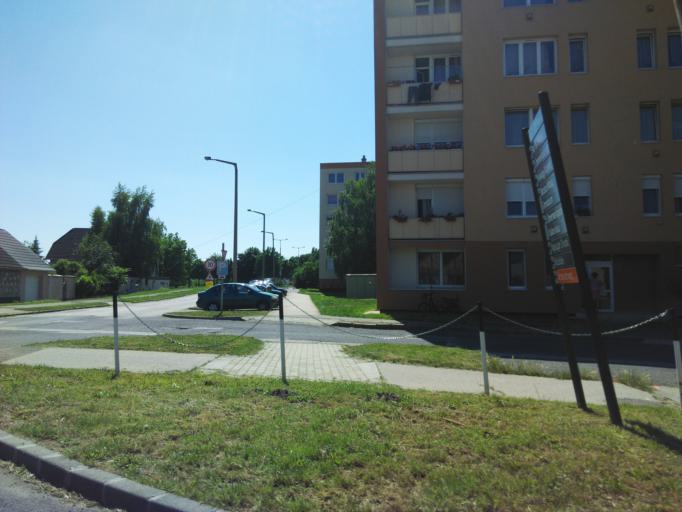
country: HU
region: Fejer
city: Mor
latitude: 47.3661
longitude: 18.2112
